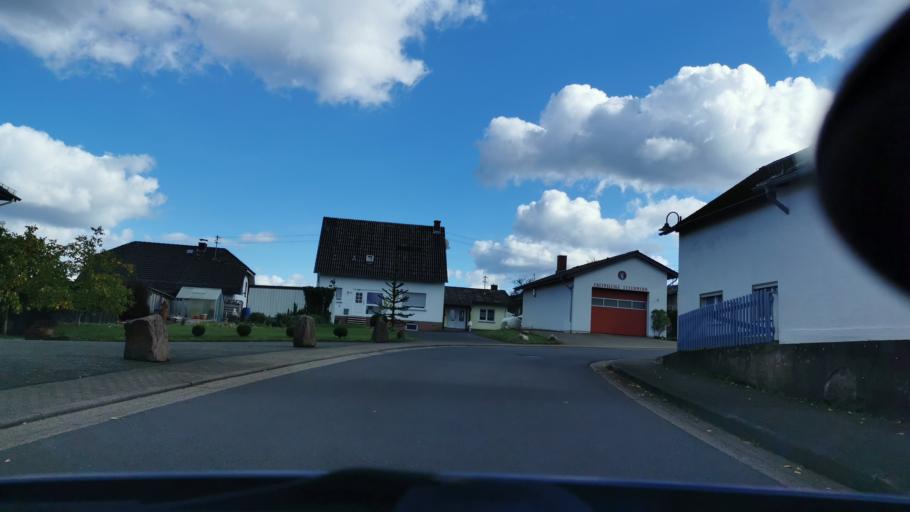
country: DE
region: Rheinland-Pfalz
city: Musweiler
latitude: 49.9949
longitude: 6.7933
